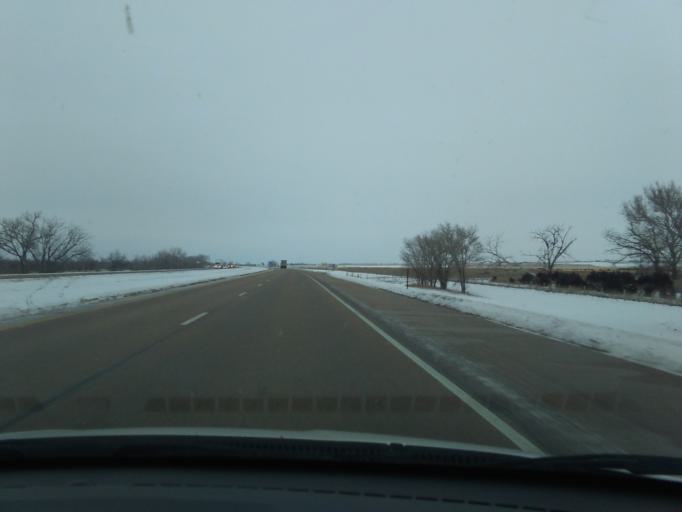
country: US
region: Nebraska
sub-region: Keith County
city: Ogallala
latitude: 41.0989
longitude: -101.7858
